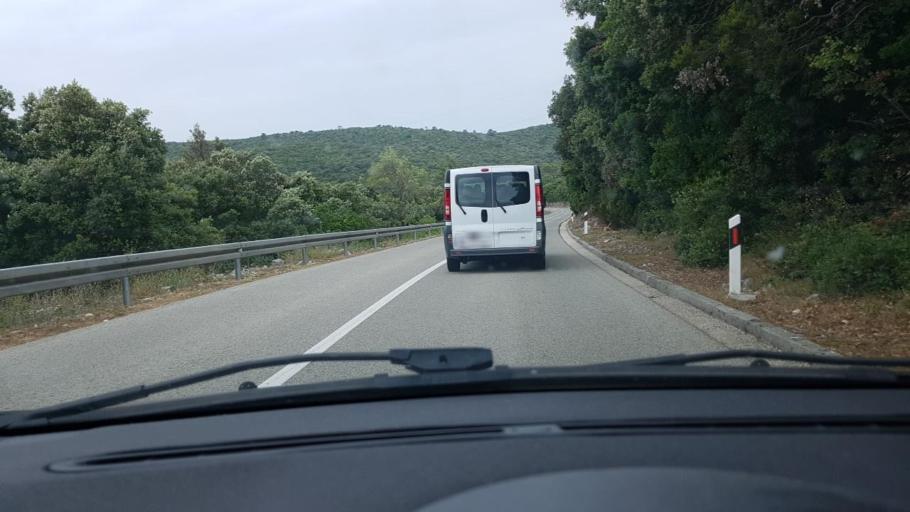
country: HR
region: Dubrovacko-Neretvanska
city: Smokvica
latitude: 42.9453
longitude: 17.0029
